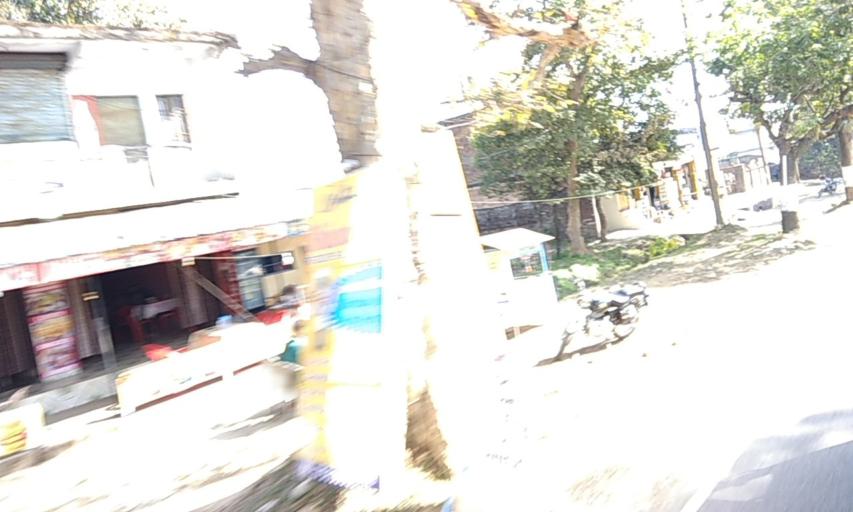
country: IN
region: Himachal Pradesh
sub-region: Kangra
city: Yol
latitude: 32.2169
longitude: 76.1792
